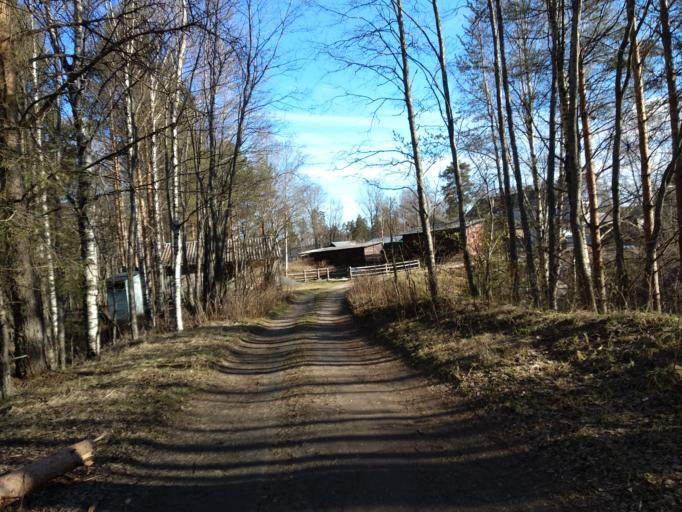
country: RU
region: Republic of Karelia
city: Girvas
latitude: 62.4840
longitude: 33.6782
